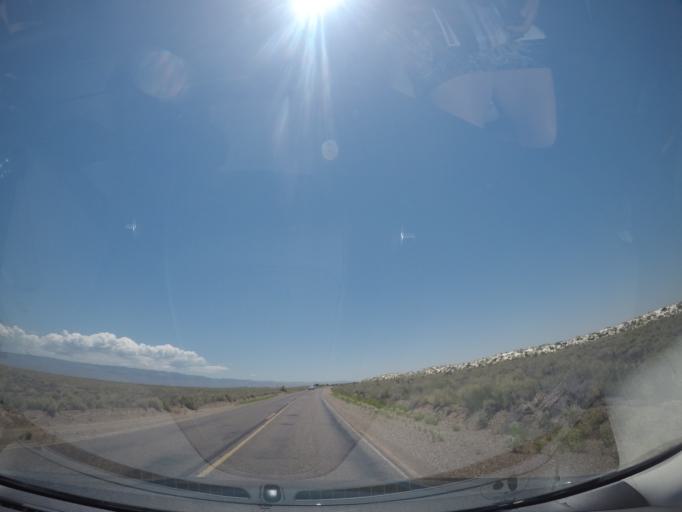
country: US
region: New Mexico
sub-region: Otero County
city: Holloman Air Force Base
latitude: 32.7855
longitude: -106.1809
